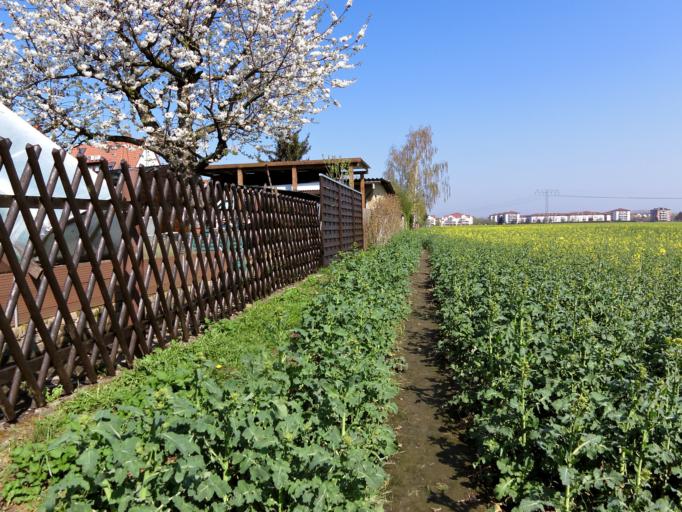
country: DE
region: Saxony
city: Leipzig
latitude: 51.3828
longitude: 12.3349
